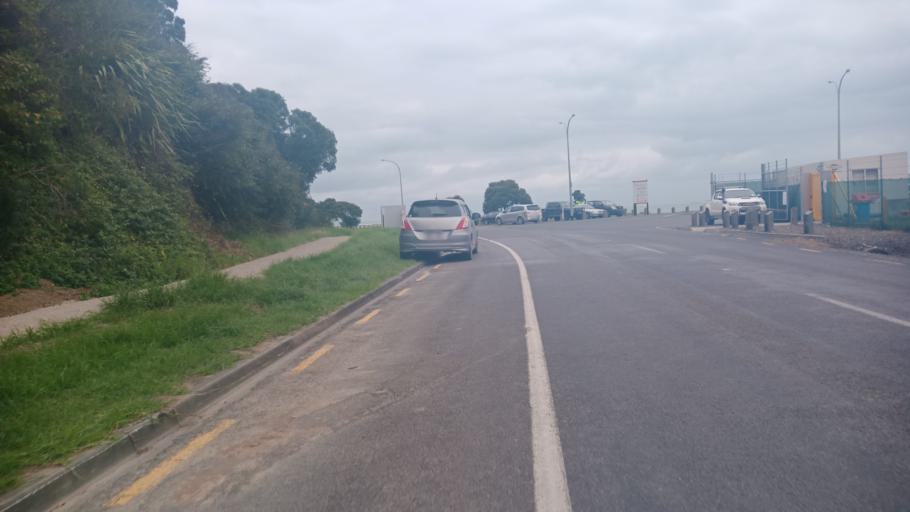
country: NZ
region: Gisborne
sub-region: Gisborne District
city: Gisborne
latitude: -38.6794
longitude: 178.0271
